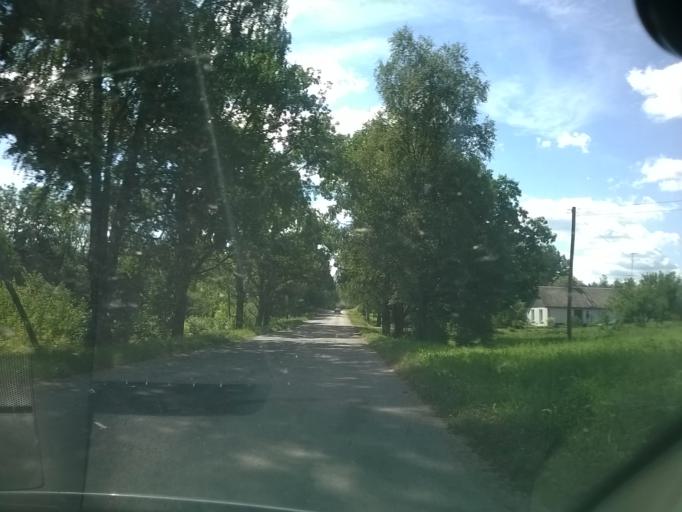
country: LV
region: Aluksnes Rajons
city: Aluksne
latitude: 57.4400
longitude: 27.0371
